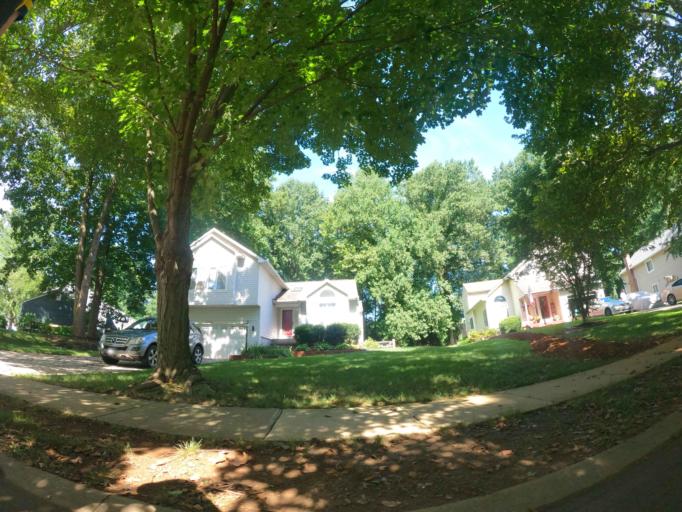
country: US
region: Maryland
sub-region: Howard County
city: Savage
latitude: 39.1516
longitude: -76.8373
